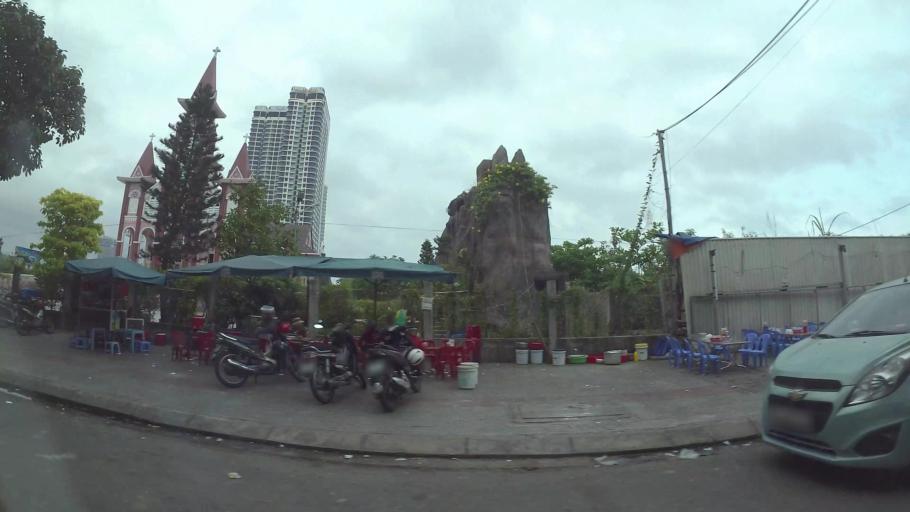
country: VN
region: Da Nang
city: Son Tra
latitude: 16.0687
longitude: 108.2301
